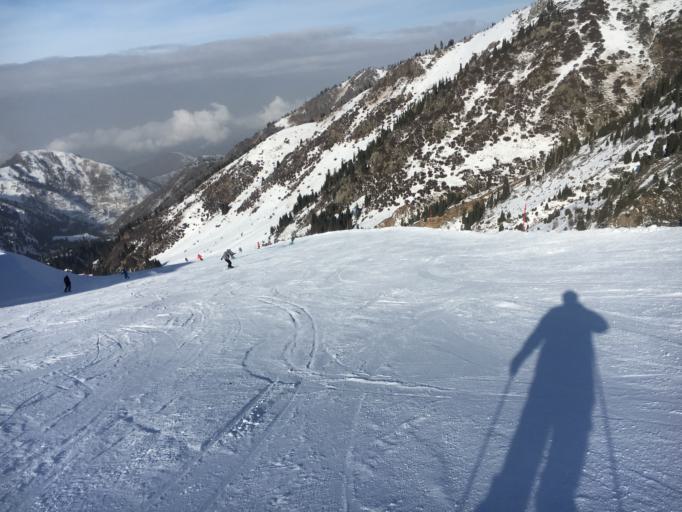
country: KZ
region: Almaty Qalasy
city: Almaty
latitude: 43.1218
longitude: 77.0948
